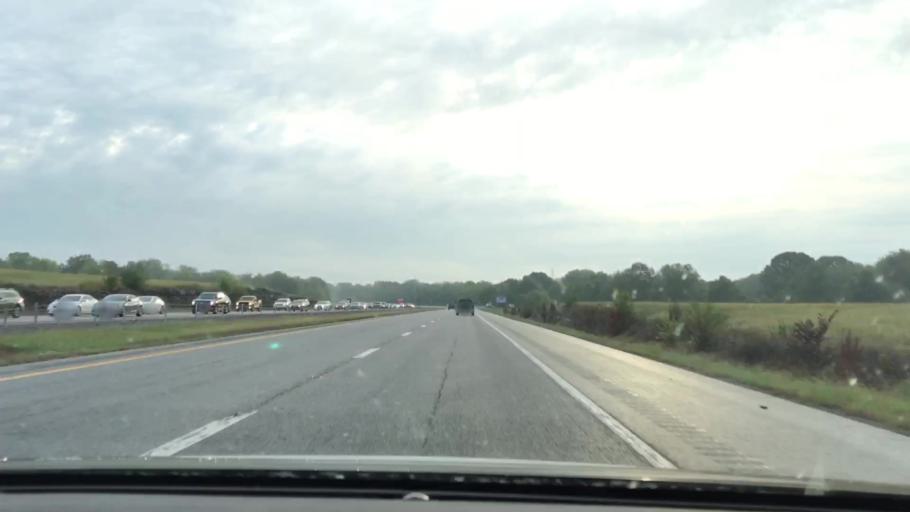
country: US
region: Tennessee
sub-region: Sumner County
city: Hendersonville
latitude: 36.3302
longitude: -86.6185
